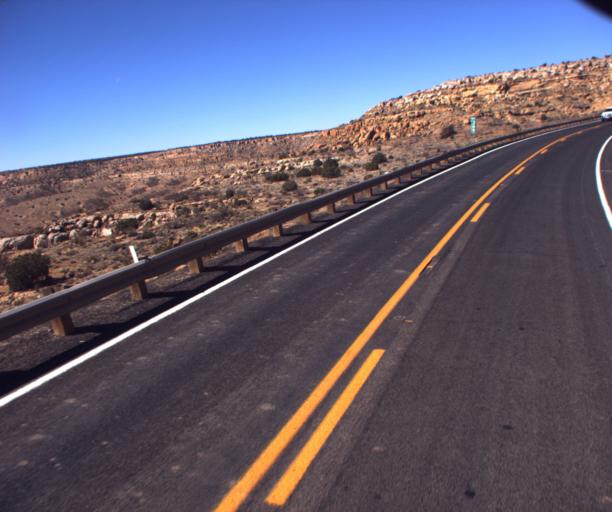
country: US
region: Arizona
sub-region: Navajo County
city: First Mesa
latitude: 35.8957
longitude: -110.6634
